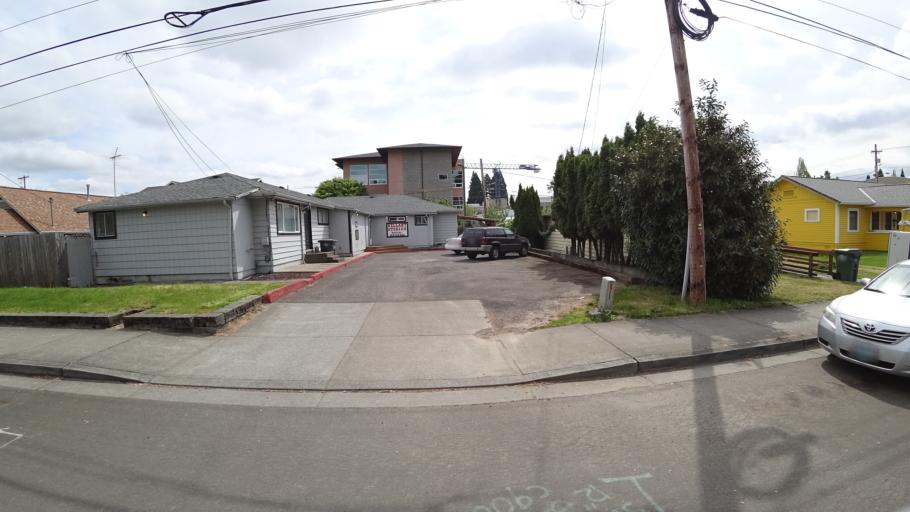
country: US
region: Oregon
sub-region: Washington County
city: Hillsboro
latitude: 45.5234
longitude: -122.9929
